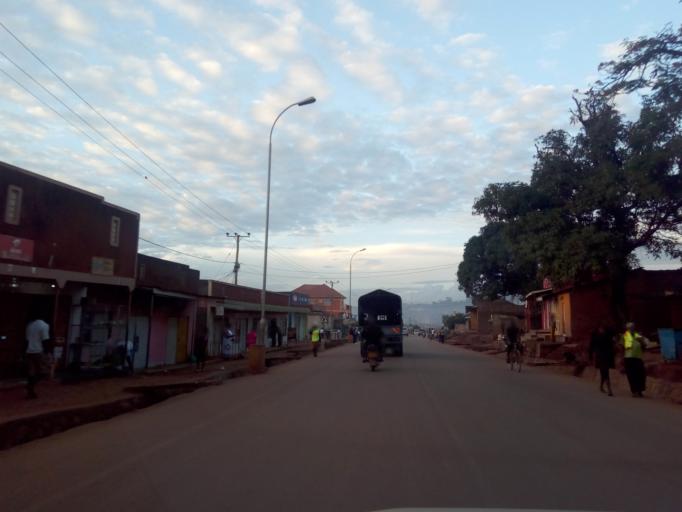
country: UG
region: Central Region
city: Kampala Central Division
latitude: 0.3591
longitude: 32.5699
